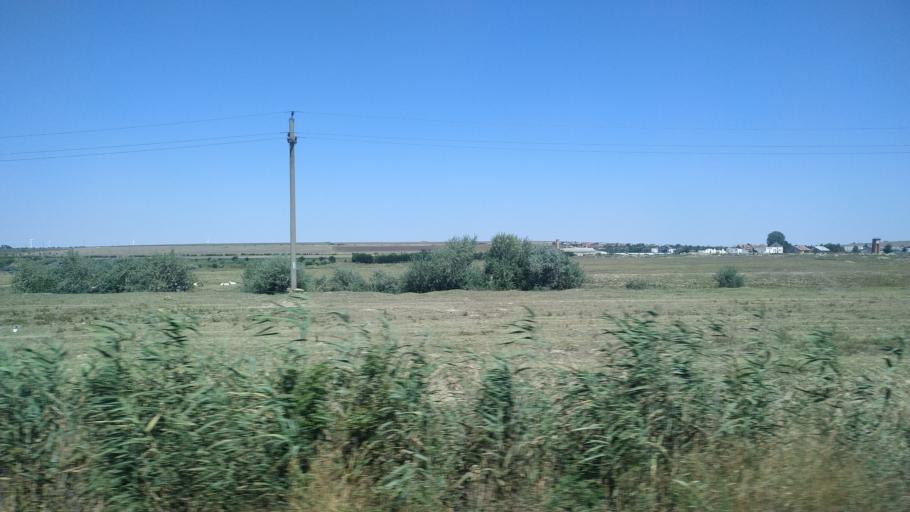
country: RO
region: Constanta
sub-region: Comuna Mircea Voda
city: Satu Nou
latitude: 44.2601
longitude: 28.2110
